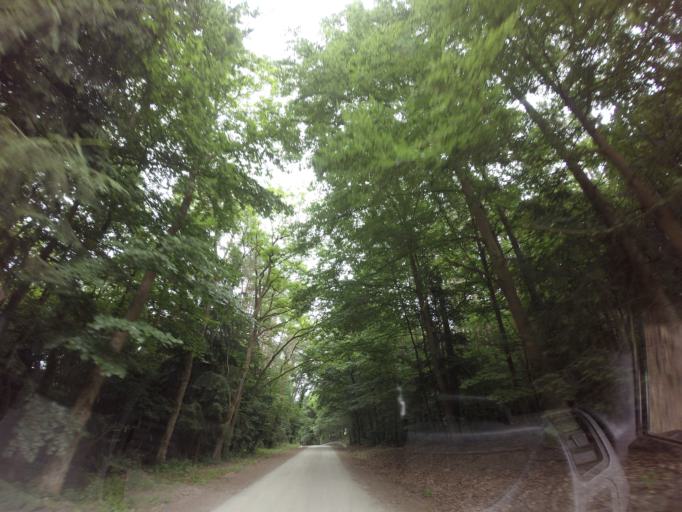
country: PL
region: Lubusz
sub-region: Powiat strzelecko-drezdenecki
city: Stare Kurowo
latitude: 52.9025
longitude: 15.6614
